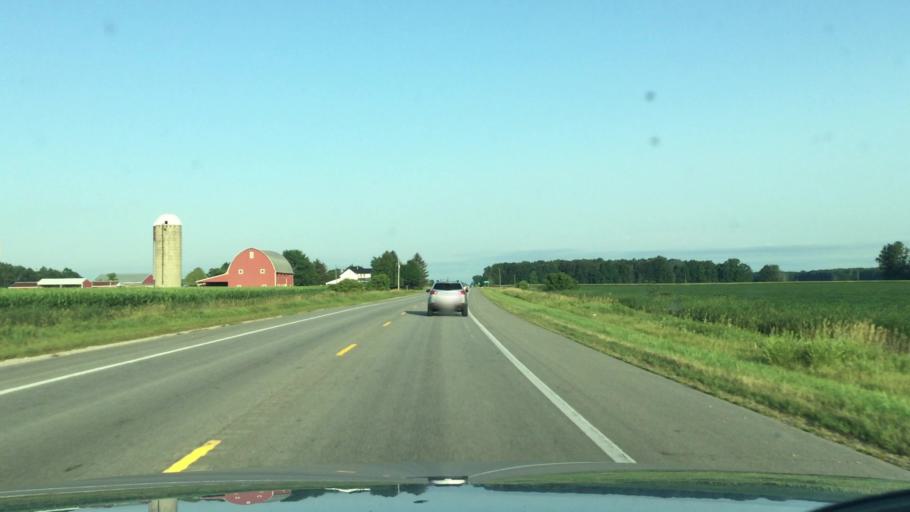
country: US
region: Michigan
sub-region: Montcalm County
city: Carson City
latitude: 43.1761
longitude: -84.7214
